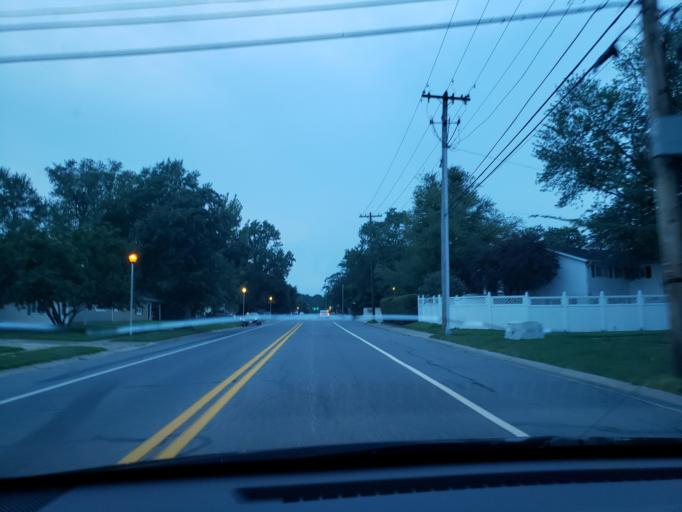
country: US
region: Delaware
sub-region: Kent County
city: Rodney Village
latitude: 39.1330
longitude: -75.5328
